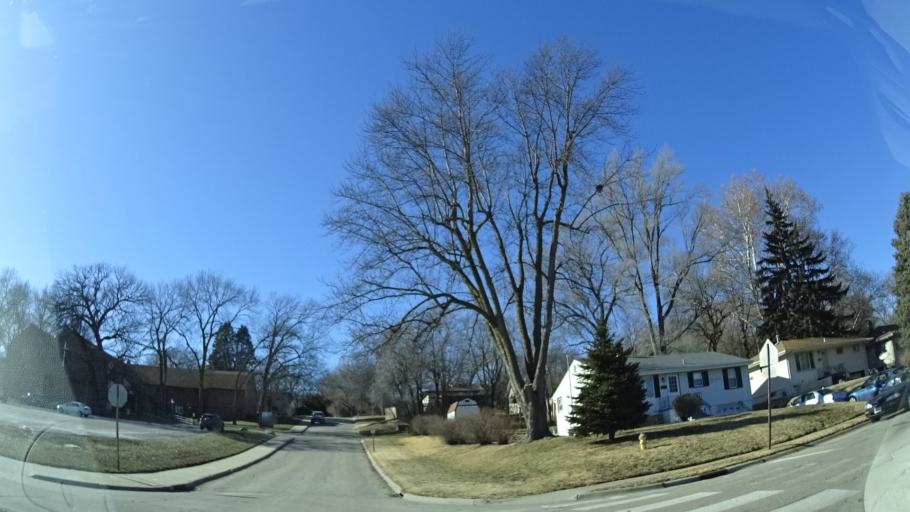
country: US
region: Nebraska
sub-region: Sarpy County
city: Bellevue
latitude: 41.1448
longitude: -95.8921
